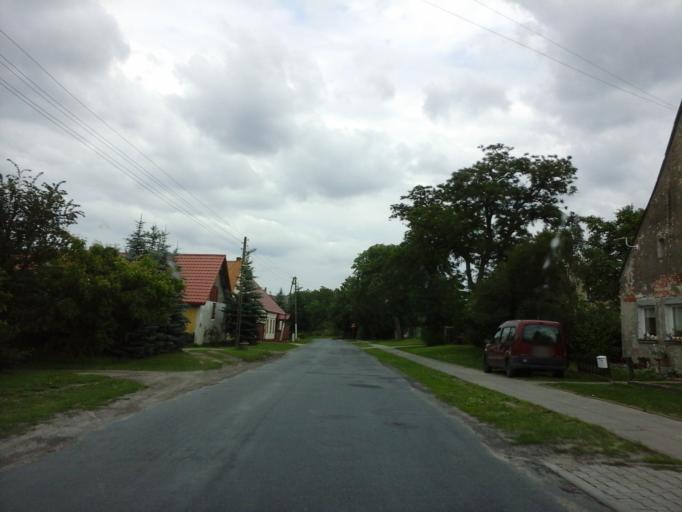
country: PL
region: West Pomeranian Voivodeship
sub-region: Powiat stargardzki
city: Dolice
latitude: 53.2543
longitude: 15.1938
